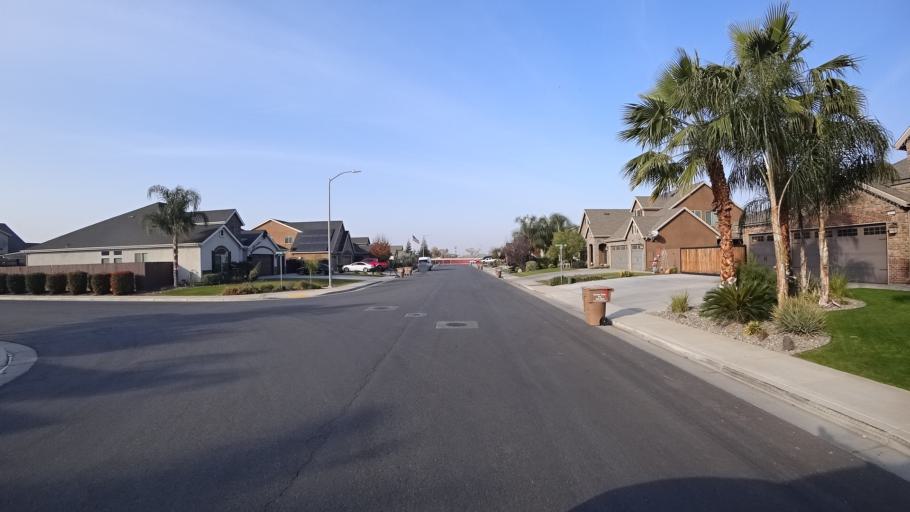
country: US
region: California
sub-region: Kern County
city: Greenacres
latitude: 35.4320
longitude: -119.1073
